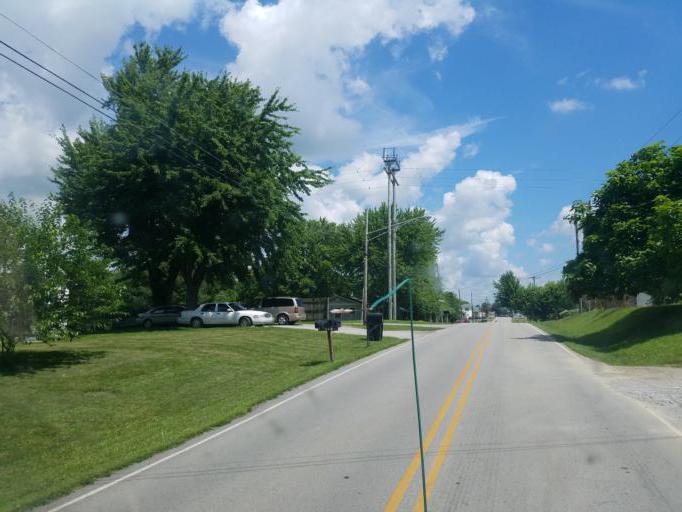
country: US
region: Kentucky
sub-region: Grayson County
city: Leitchfield
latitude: 37.4916
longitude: -86.2255
